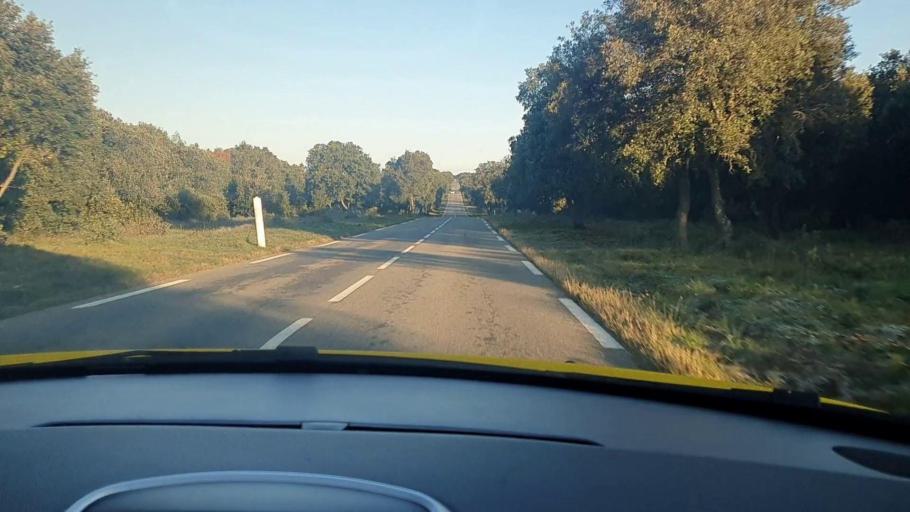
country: FR
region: Languedoc-Roussillon
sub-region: Departement du Gard
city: Montaren-et-Saint-Mediers
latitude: 44.0909
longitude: 4.3891
